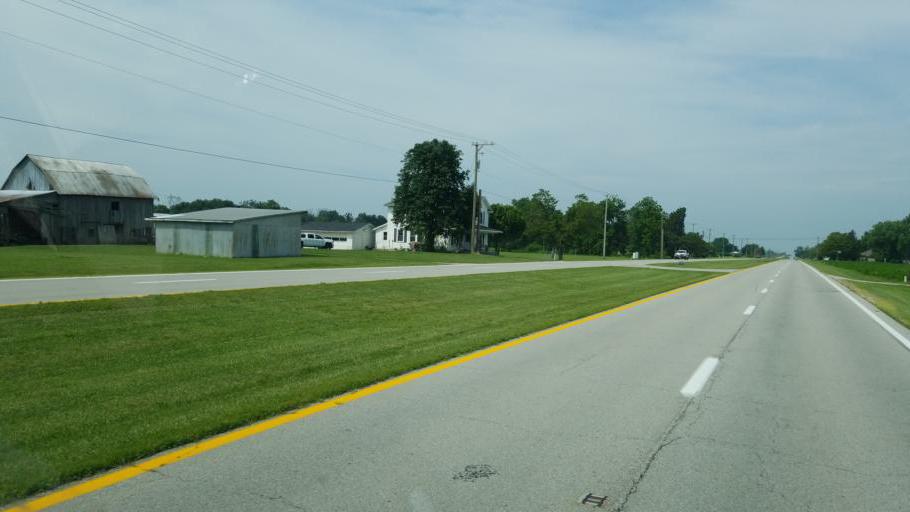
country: US
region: Ohio
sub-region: Madison County
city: West Jefferson
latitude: 39.9405
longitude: -83.3506
